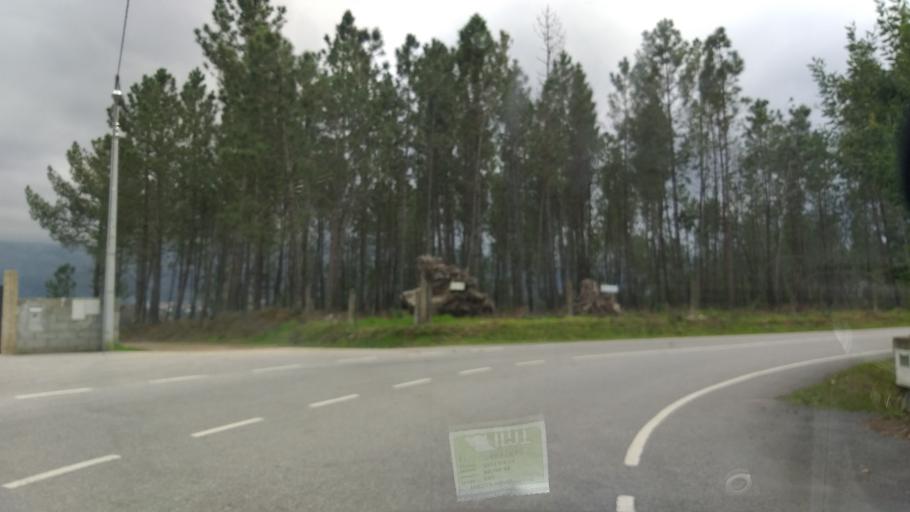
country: PT
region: Guarda
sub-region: Seia
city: Seia
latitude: 40.4783
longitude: -7.6644
